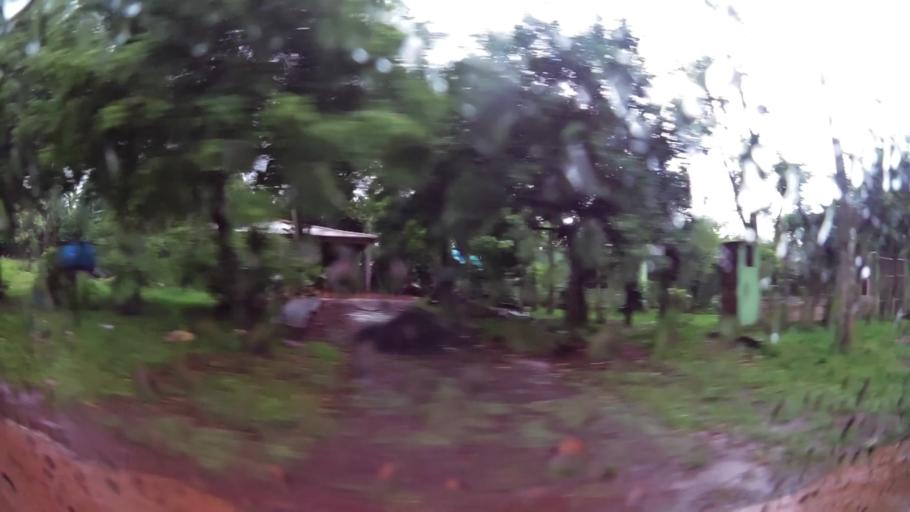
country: PY
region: Alto Parana
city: Presidente Franco
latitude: -25.5446
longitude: -54.6779
